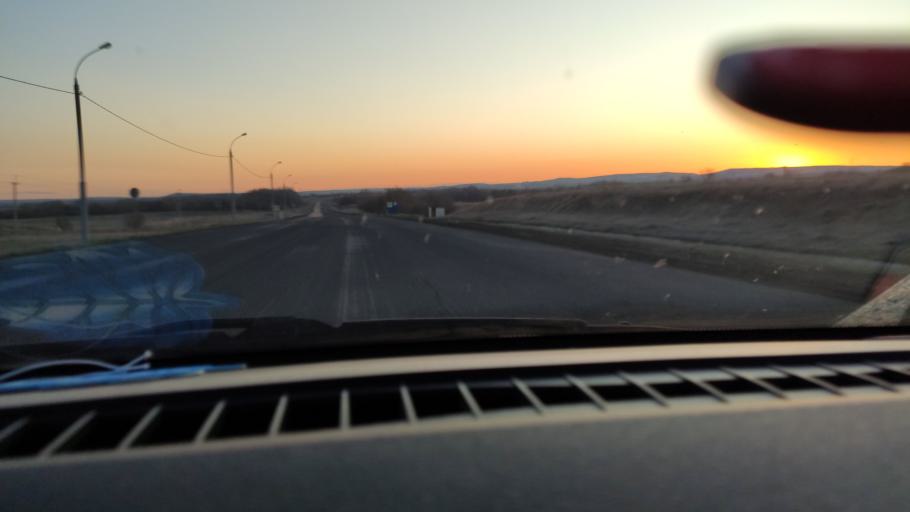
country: RU
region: Saratov
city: Yelshanka
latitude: 51.8167
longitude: 46.2116
